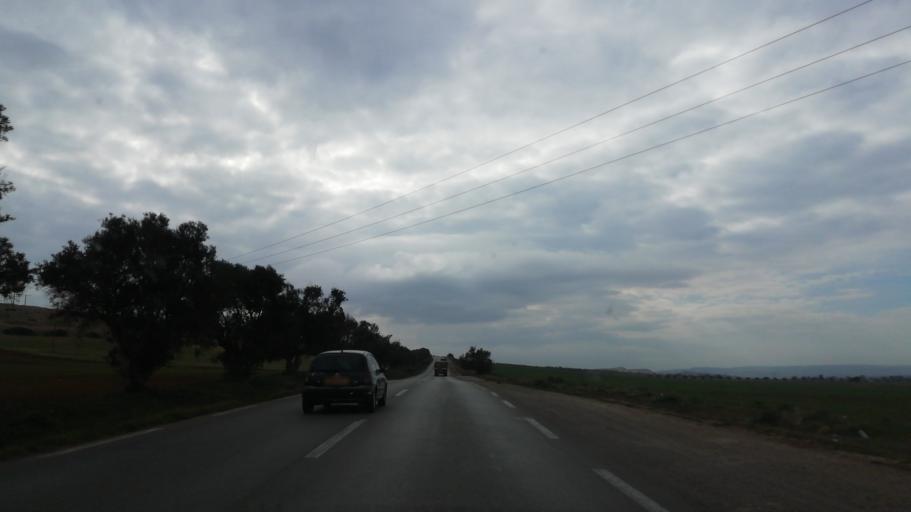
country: DZ
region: Oran
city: Ain el Bya
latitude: 35.7397
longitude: -0.3550
